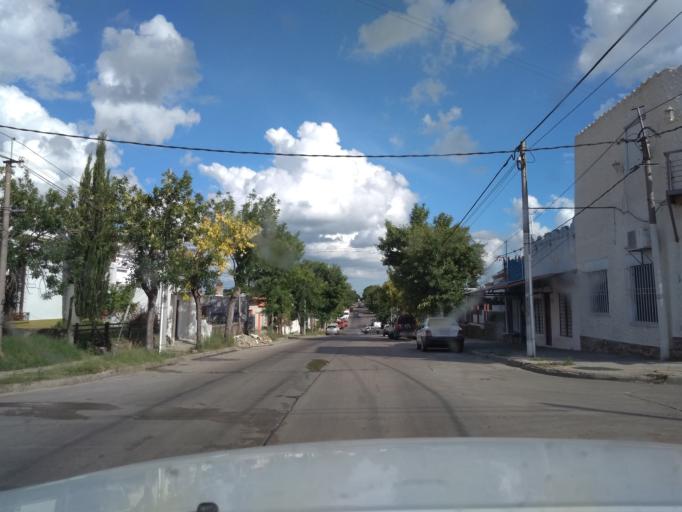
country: UY
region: Florida
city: Florida
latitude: -34.0926
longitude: -56.2149
